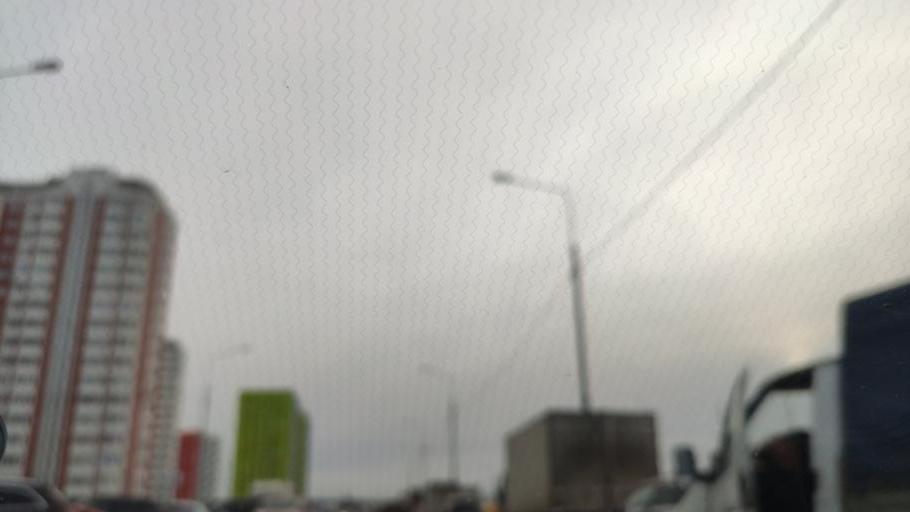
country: RU
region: Moscow
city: Annino
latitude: 55.5337
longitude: 37.6129
